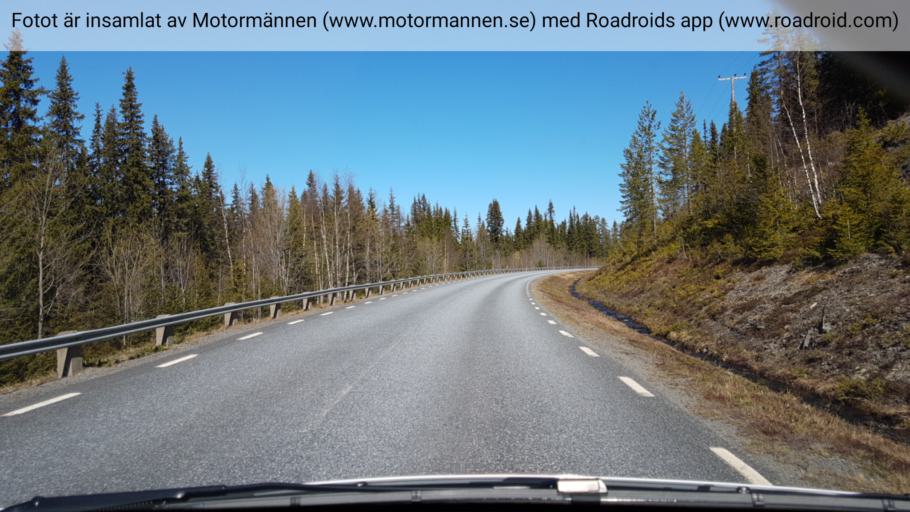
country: SE
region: Vaesterbotten
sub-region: Vilhelmina Kommun
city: Sjoberg
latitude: 64.9546
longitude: 15.8614
